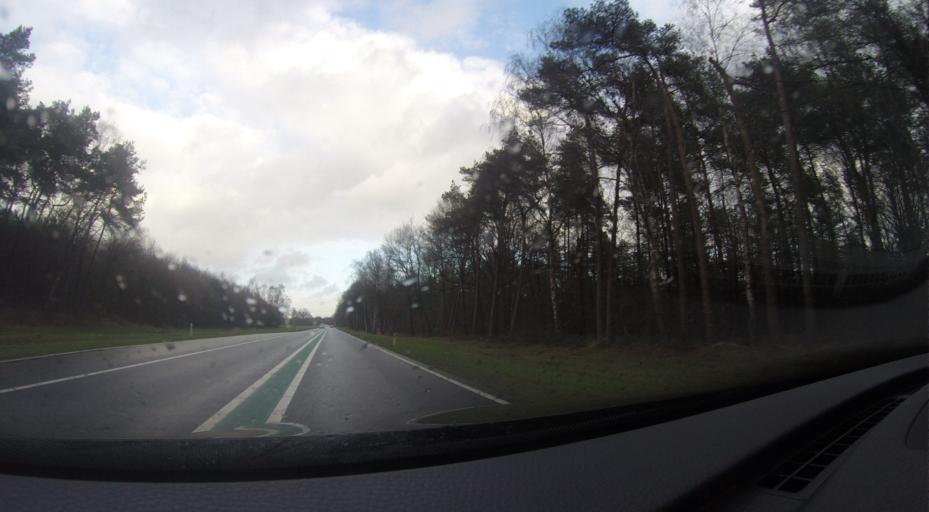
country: NL
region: Gelderland
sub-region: Gemeente Lochem
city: Laren
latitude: 52.2143
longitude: 6.3850
